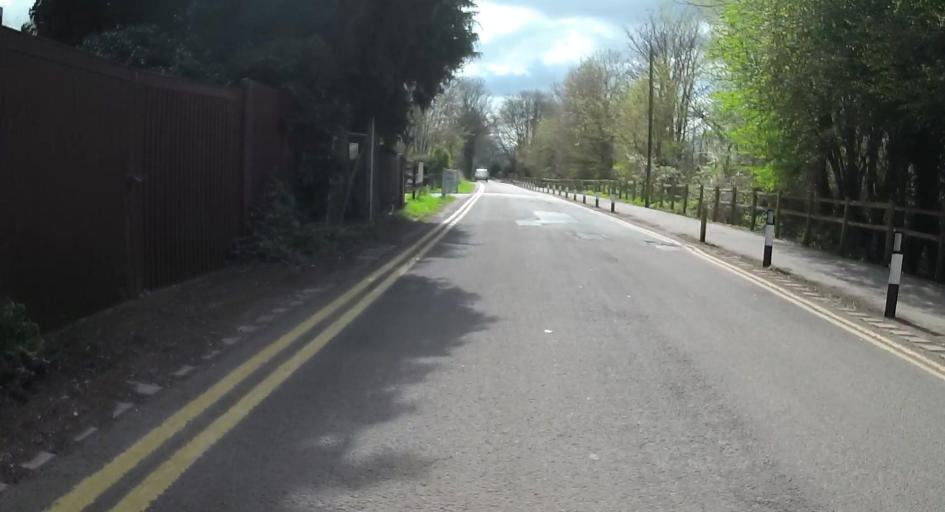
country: GB
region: England
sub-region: Surrey
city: Shepperton
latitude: 51.3869
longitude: -0.4583
